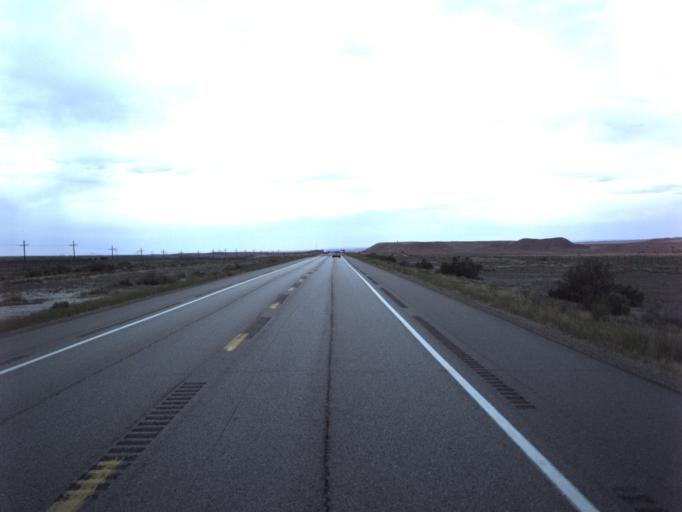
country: US
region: Utah
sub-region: Carbon County
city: East Carbon City
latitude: 39.0941
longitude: -110.3217
